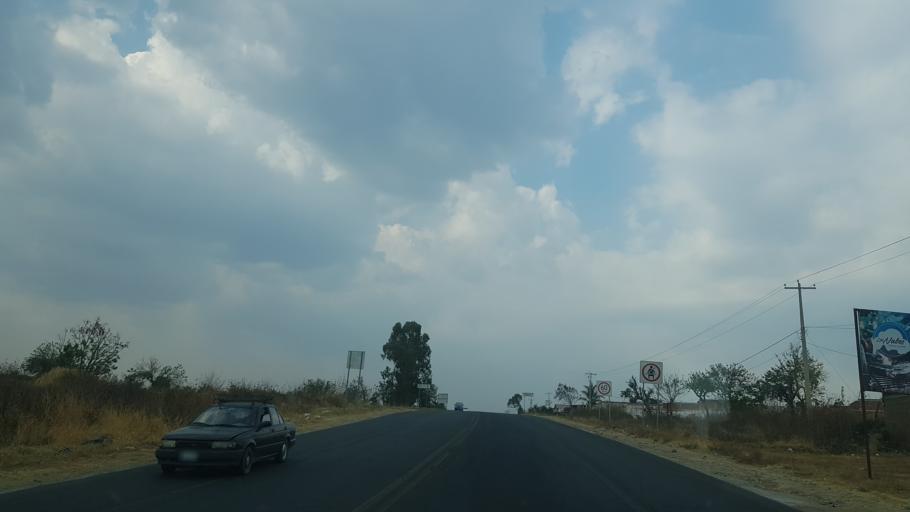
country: MX
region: Puebla
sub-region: Santa Isabel Cholula
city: Santa Ana Acozautla
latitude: 18.9696
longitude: -98.3819
